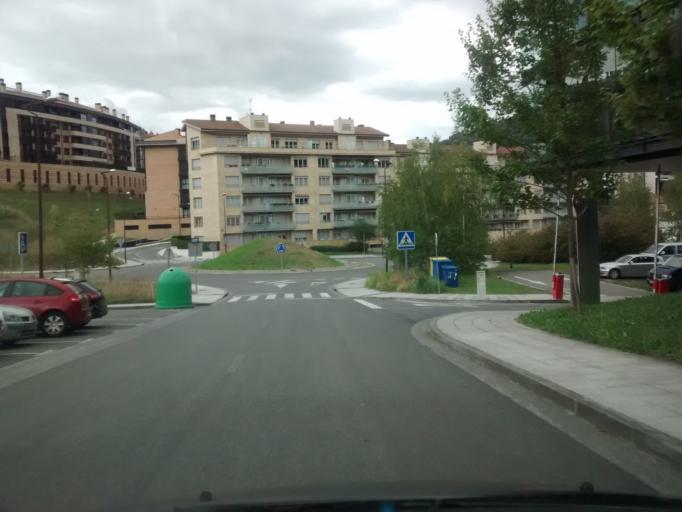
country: ES
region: Basque Country
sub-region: Provincia de Guipuzcoa
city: Arrasate / Mondragon
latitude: 43.0627
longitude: -2.5050
